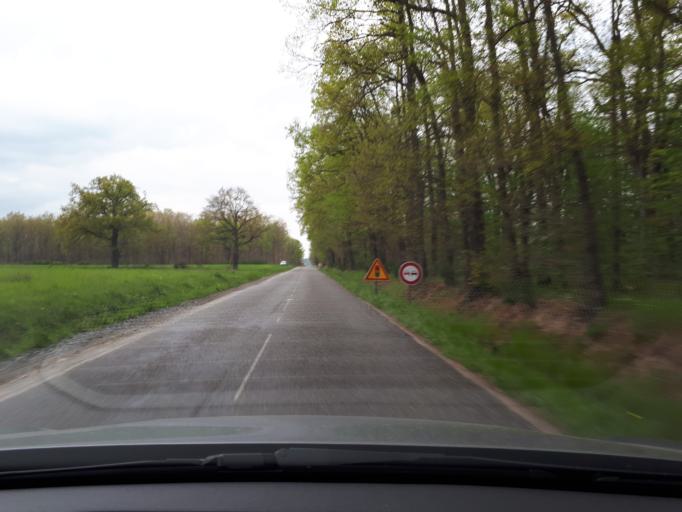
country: FR
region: Rhone-Alpes
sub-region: Departement de la Loire
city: Feurs
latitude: 45.7238
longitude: 4.2924
